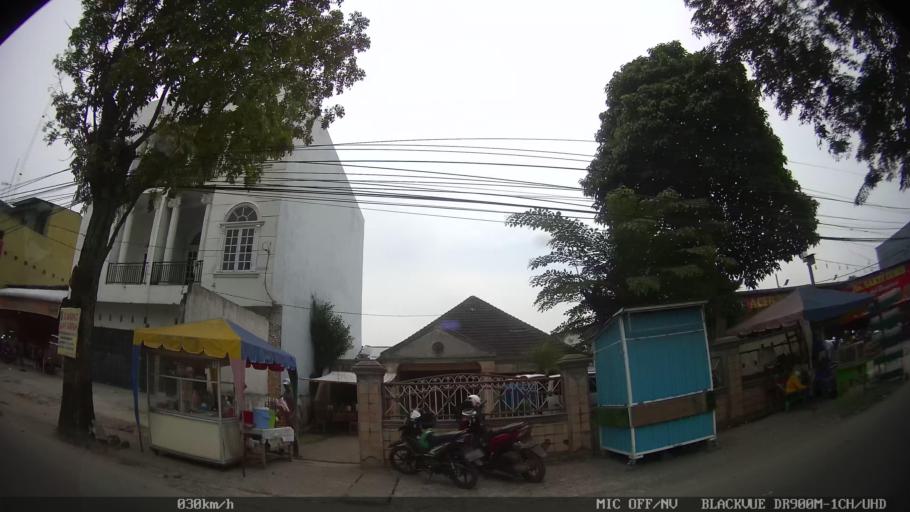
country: ID
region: North Sumatra
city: Medan
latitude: 3.5533
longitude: 98.6930
